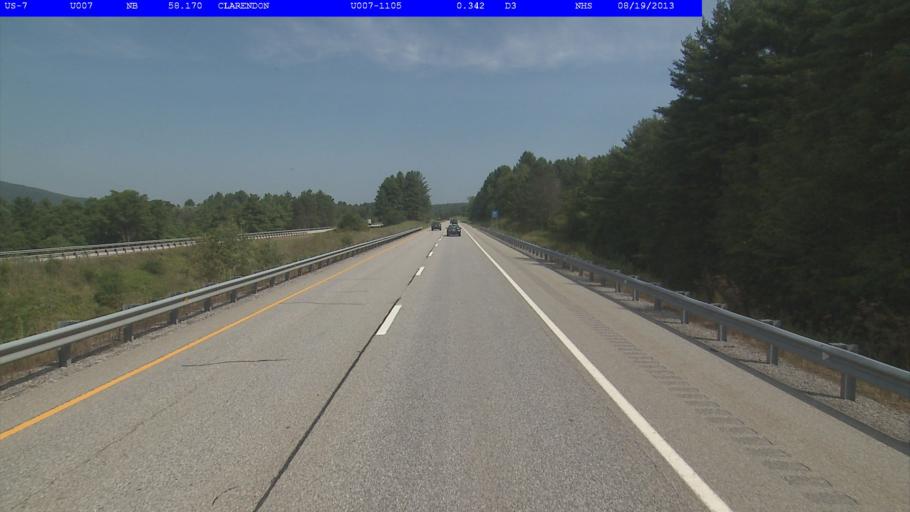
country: US
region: Vermont
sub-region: Rutland County
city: Rutland
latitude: 43.4990
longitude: -72.9682
